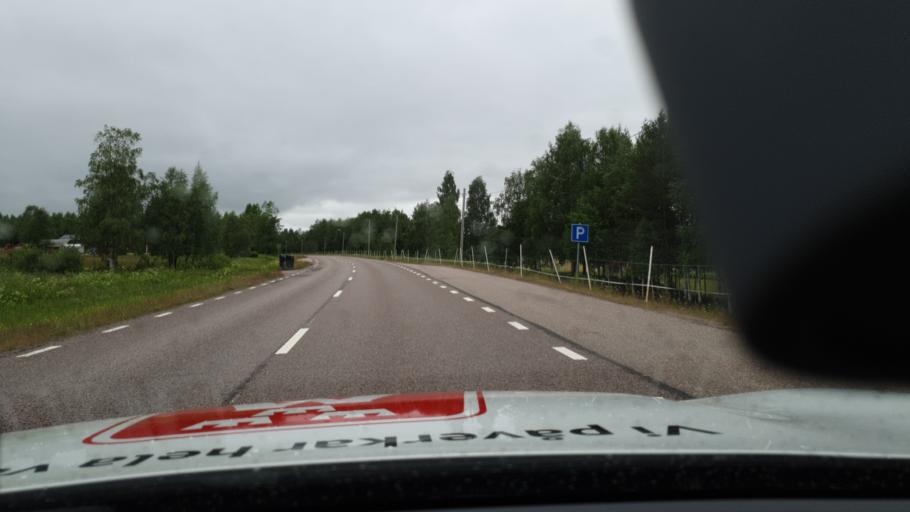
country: FI
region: Lapland
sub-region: Torniolaakso
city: Pello
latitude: 66.9550
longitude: 23.8421
